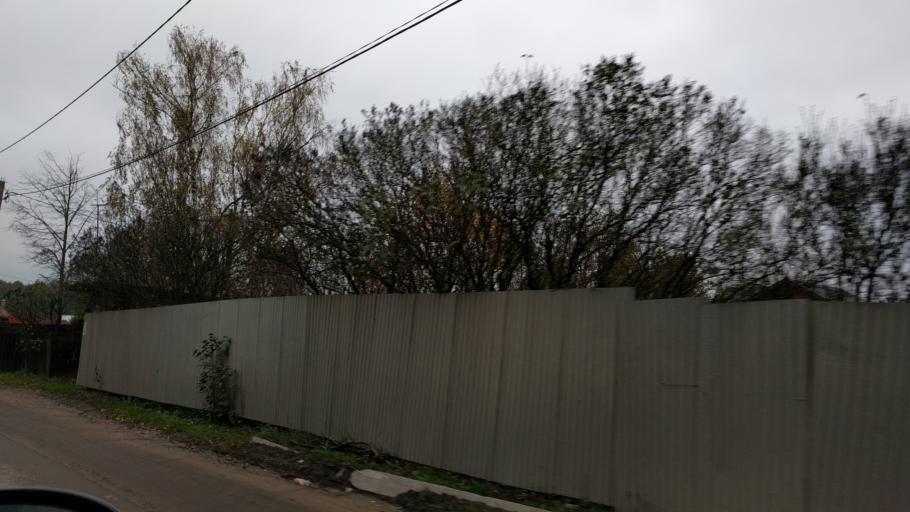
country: RU
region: Moskovskaya
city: Selyatino
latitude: 55.5479
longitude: 36.9844
